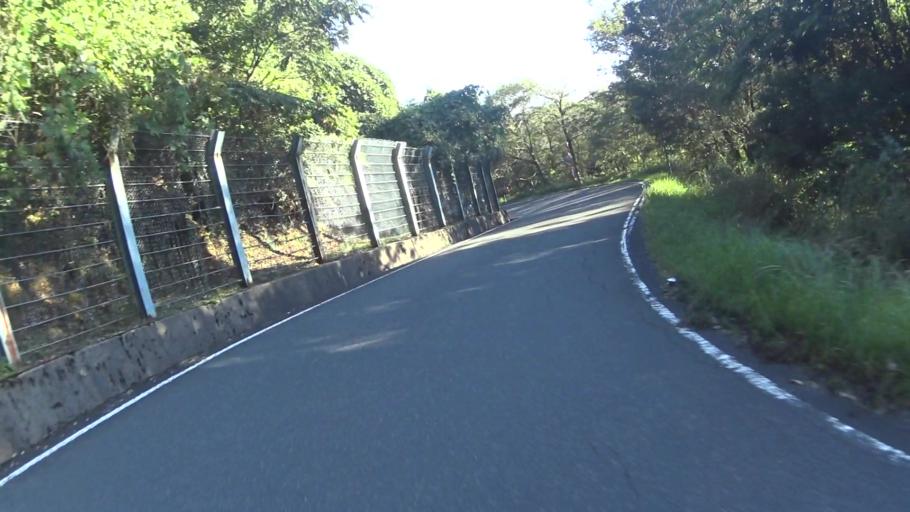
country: JP
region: Hyogo
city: Toyooka
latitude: 35.6133
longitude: 134.8795
